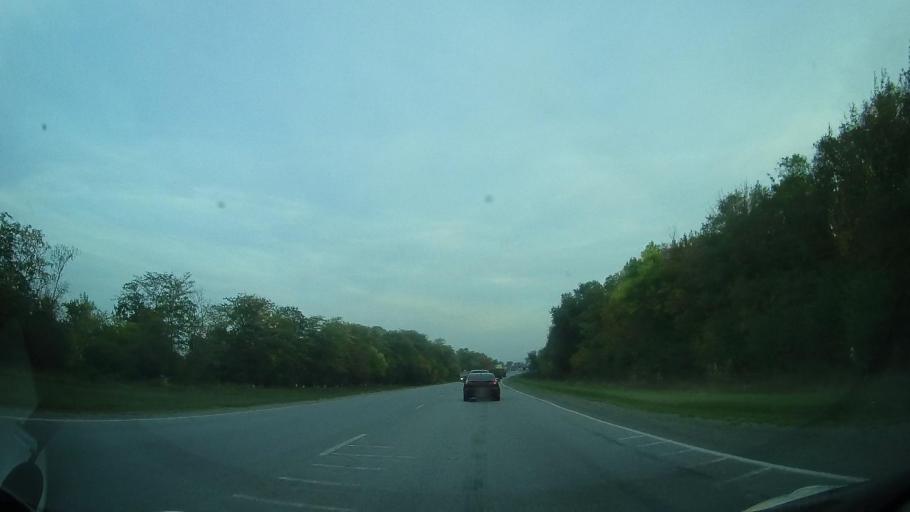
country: RU
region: Rostov
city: Kirovskaya
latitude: 46.9908
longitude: 40.0214
